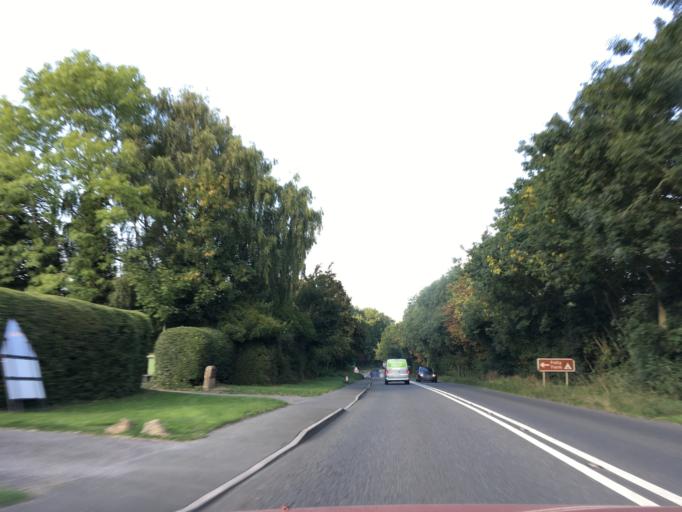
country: GB
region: England
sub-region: Gloucestershire
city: Bourton on the Water
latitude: 51.8846
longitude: -1.7721
